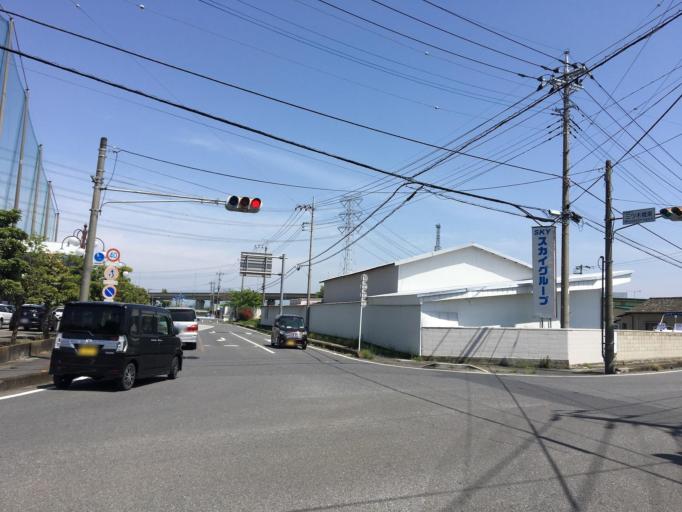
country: JP
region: Gunma
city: Sakai-nakajima
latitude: 36.2778
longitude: 139.2738
